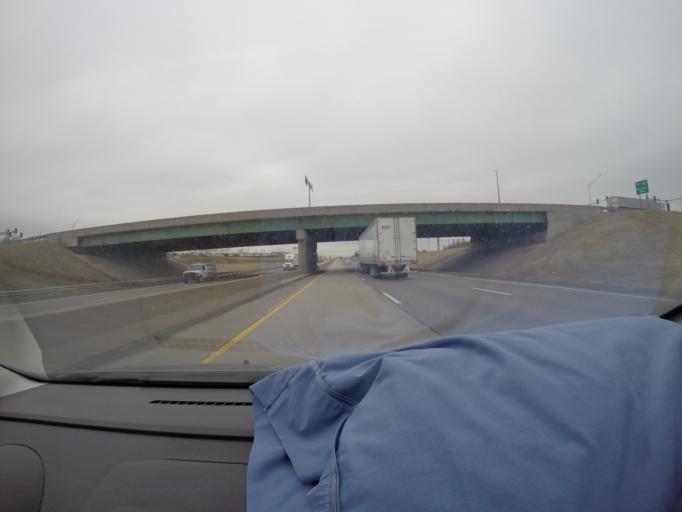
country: US
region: Missouri
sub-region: Saint Charles County
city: Dardenne Prairie
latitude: 38.8030
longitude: -90.7335
